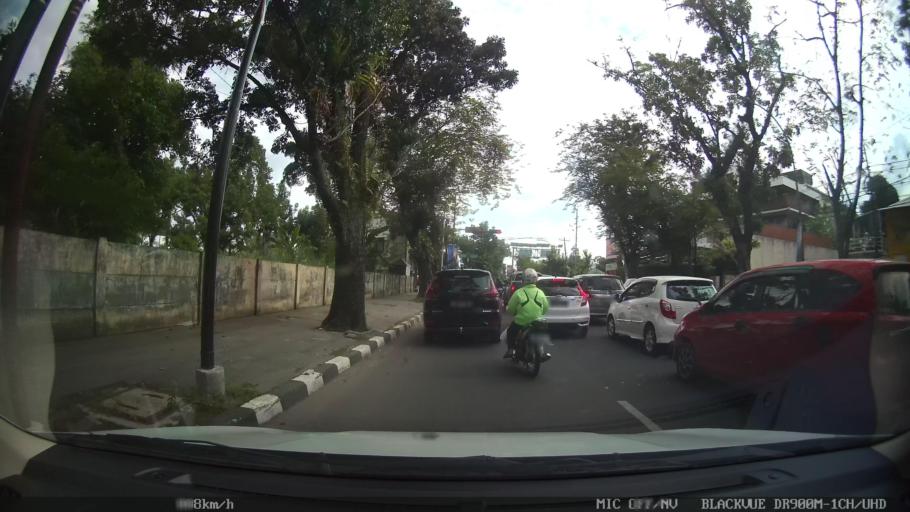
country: ID
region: North Sumatra
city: Medan
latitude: 3.5778
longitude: 98.6671
